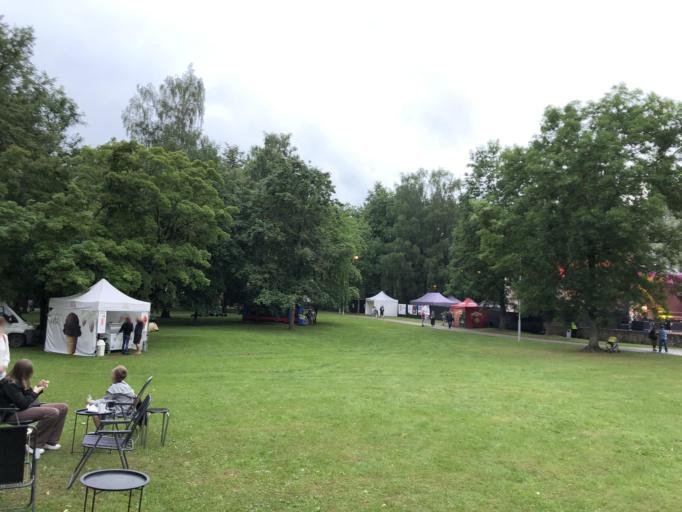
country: LV
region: Bauskas Rajons
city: Bauska
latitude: 56.4033
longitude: 24.1710
